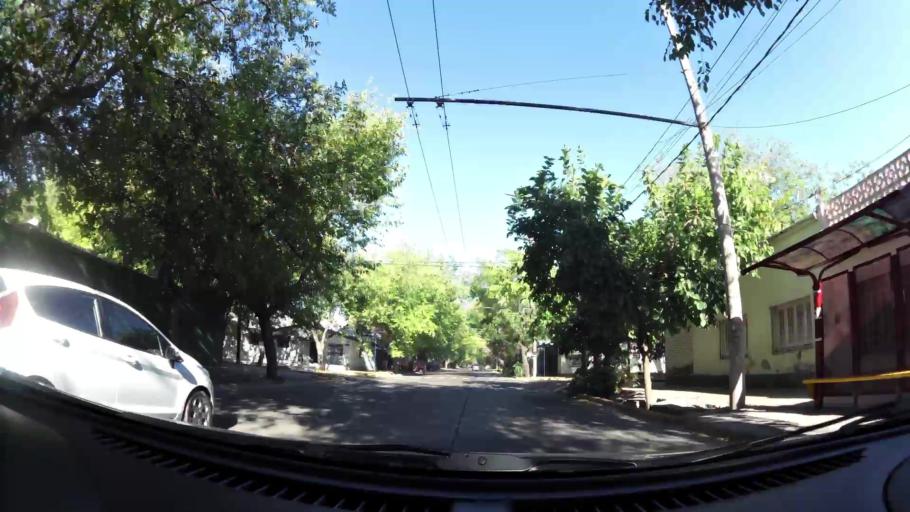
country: AR
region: Mendoza
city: Las Heras
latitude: -32.8663
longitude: -68.8494
